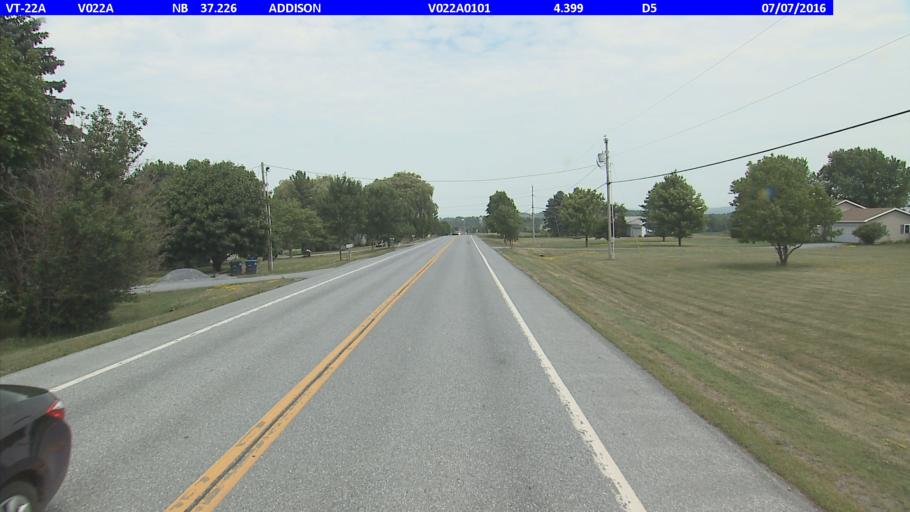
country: US
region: Vermont
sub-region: Addison County
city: Vergennes
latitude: 44.0928
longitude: -73.3014
